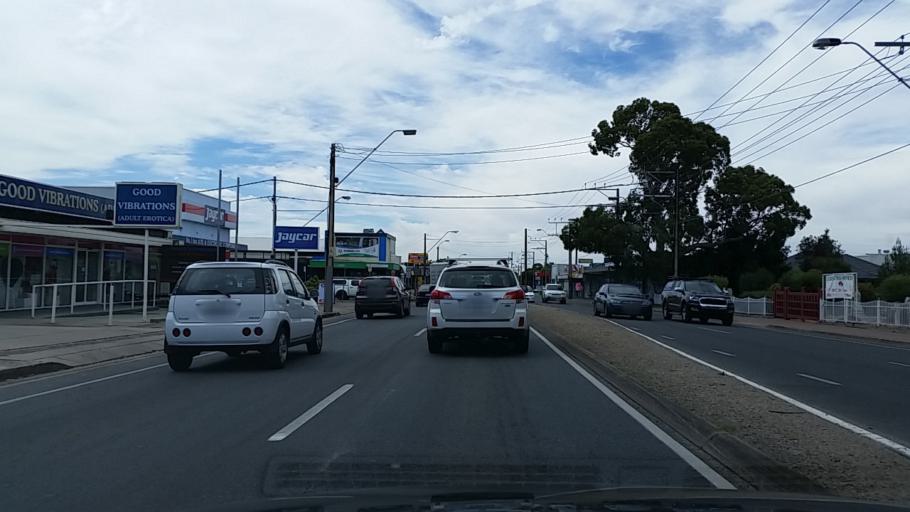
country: AU
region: South Australia
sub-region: Marion
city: Clovelly Park
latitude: -34.9966
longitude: 138.5751
